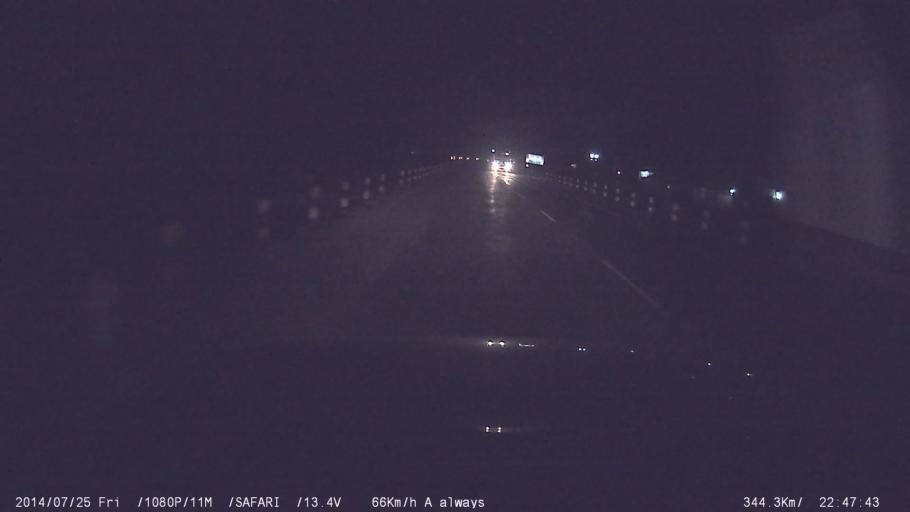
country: IN
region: Tamil Nadu
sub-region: Coimbatore
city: Irugur
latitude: 11.0174
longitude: 77.0747
